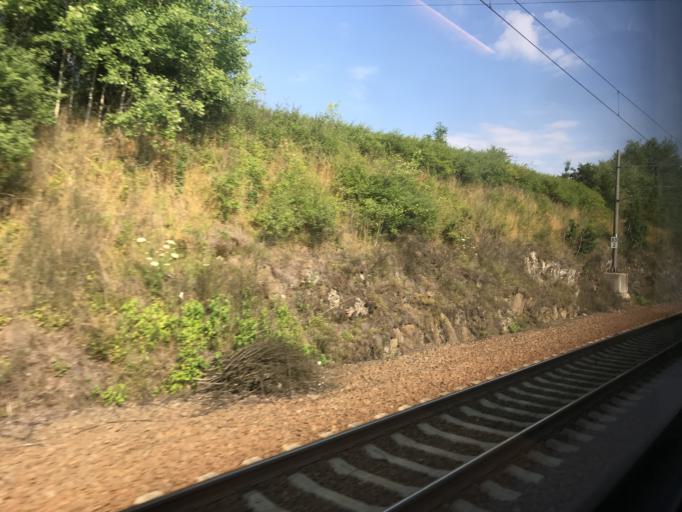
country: CZ
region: Jihocesky
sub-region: Okres Tabor
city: Tabor
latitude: 49.4247
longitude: 14.6679
